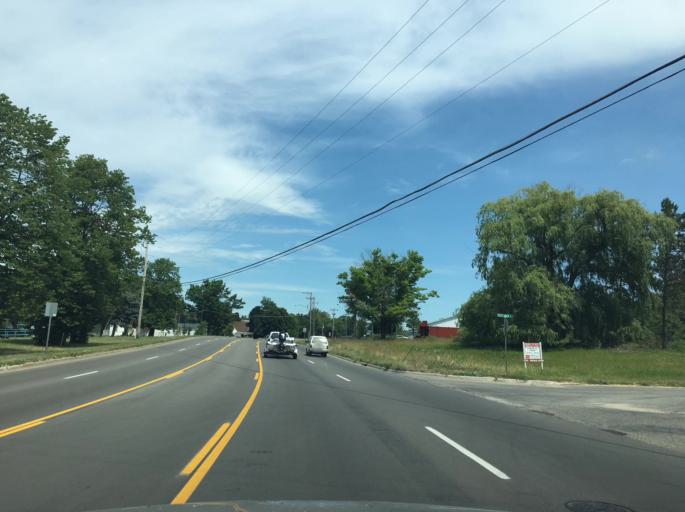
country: US
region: Michigan
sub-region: Grand Traverse County
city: Traverse City
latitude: 44.7681
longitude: -85.5038
